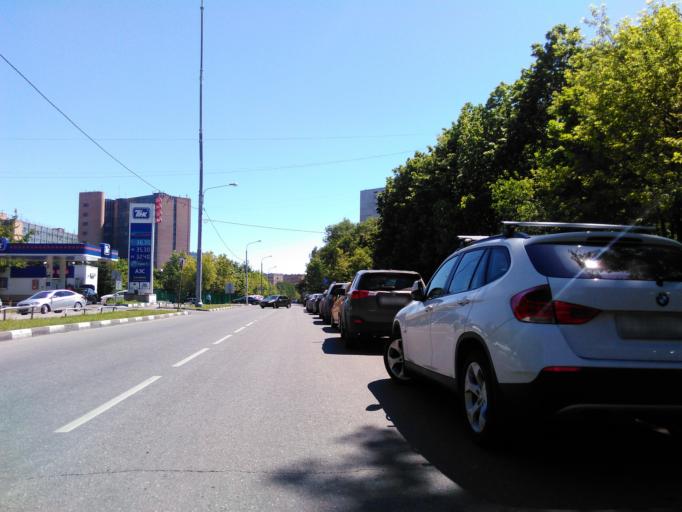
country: RU
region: Moskovskaya
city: Cheremushki
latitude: 55.6475
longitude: 37.5399
